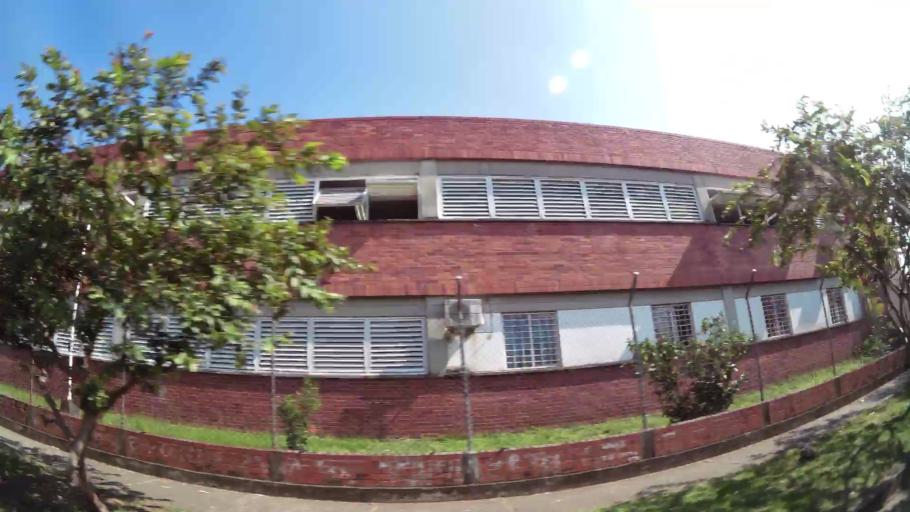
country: CO
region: Valle del Cauca
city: Cali
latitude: 3.4036
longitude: -76.5237
